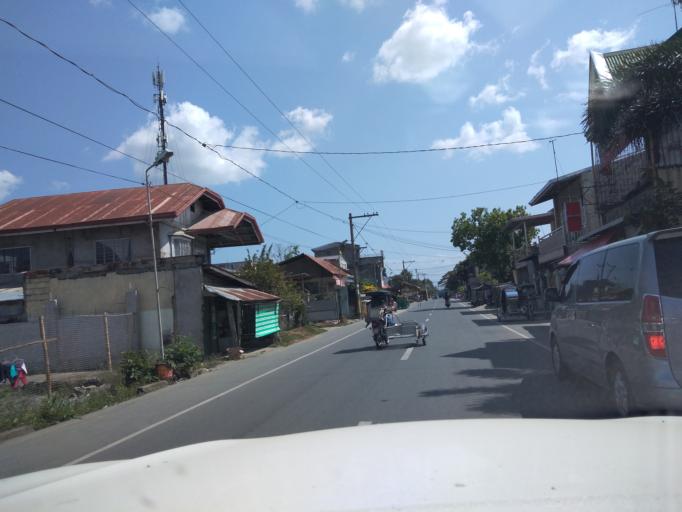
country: PH
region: Central Luzon
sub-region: Province of Pampanga
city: Bahay Pare
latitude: 15.0360
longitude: 120.8806
